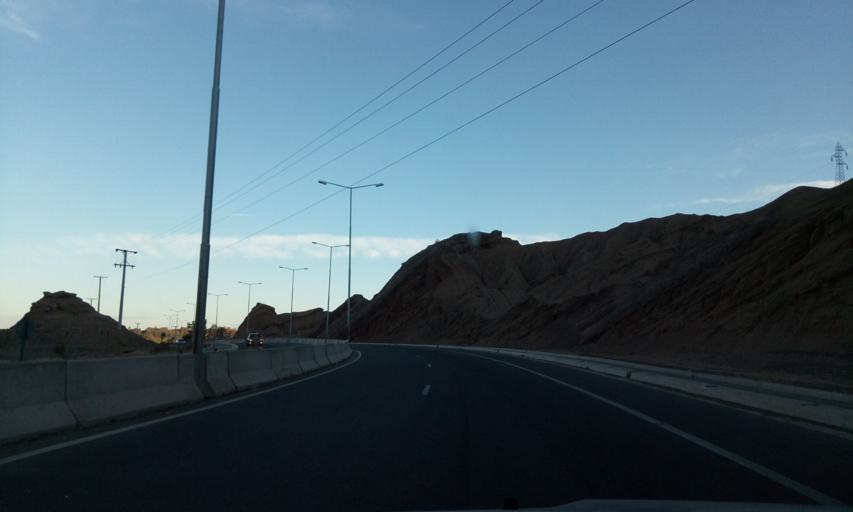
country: AR
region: San Juan
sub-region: Departamento de Rivadavia
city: Rivadavia
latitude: -31.4891
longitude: -68.6495
